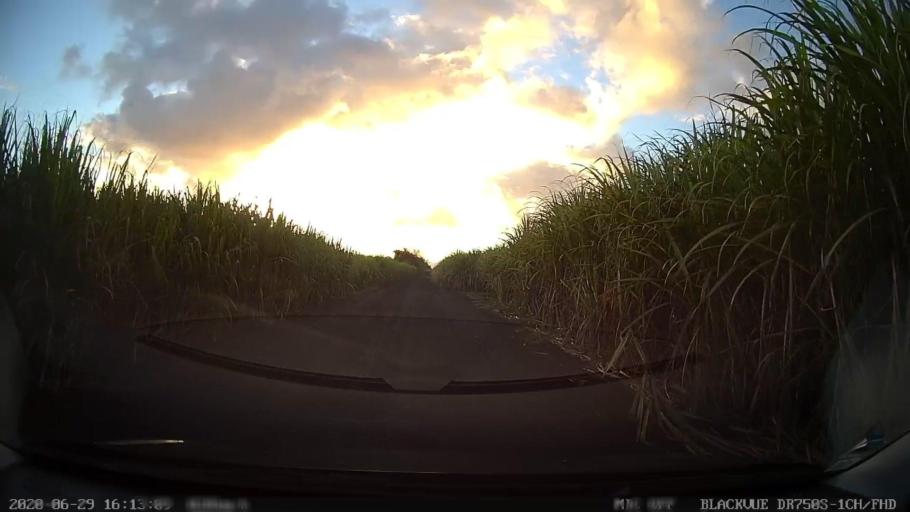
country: RE
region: Reunion
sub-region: Reunion
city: Bras-Panon
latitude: -20.9904
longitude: 55.6952
